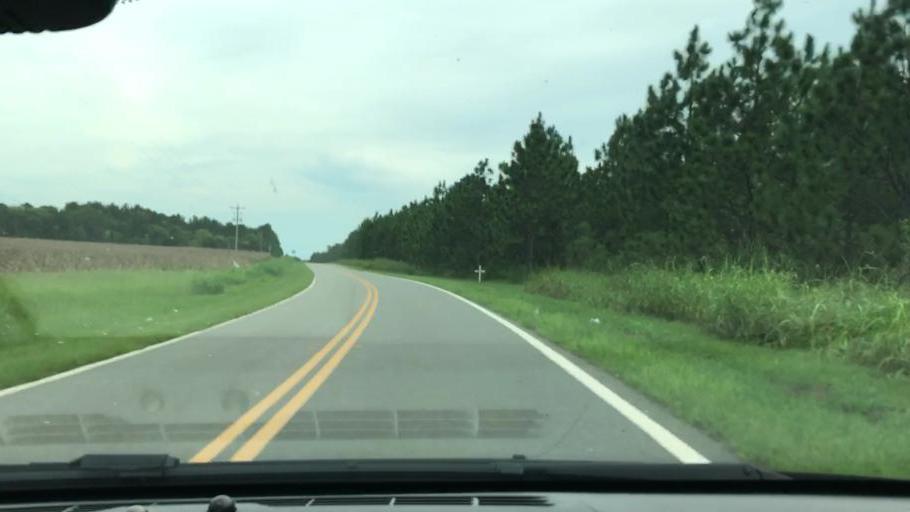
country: US
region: Georgia
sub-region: Early County
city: Blakely
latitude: 31.4272
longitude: -84.9246
